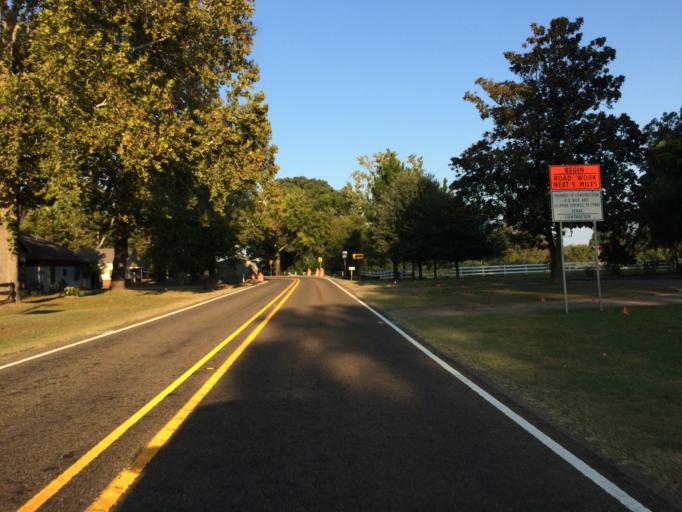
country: US
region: Texas
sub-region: Wood County
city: Quitman
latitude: 32.7173
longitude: -95.3660
